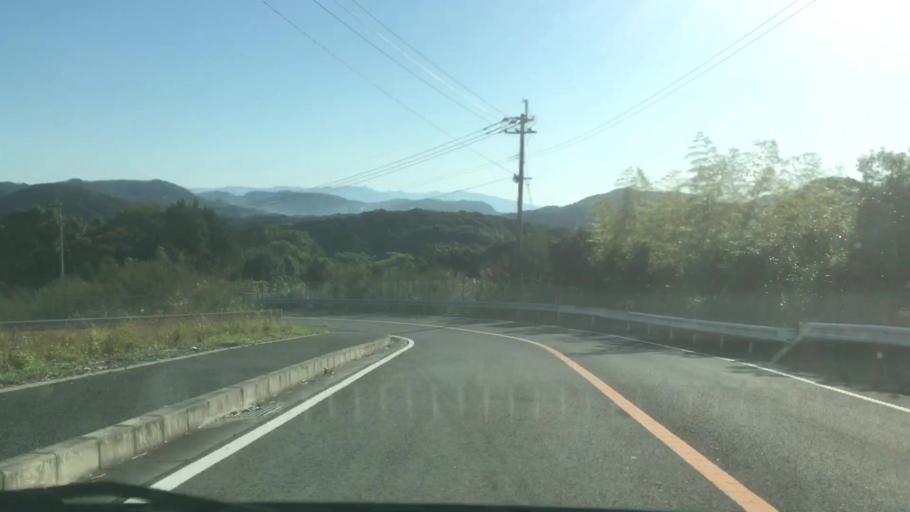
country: JP
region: Nagasaki
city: Sasebo
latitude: 32.9986
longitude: 129.7267
